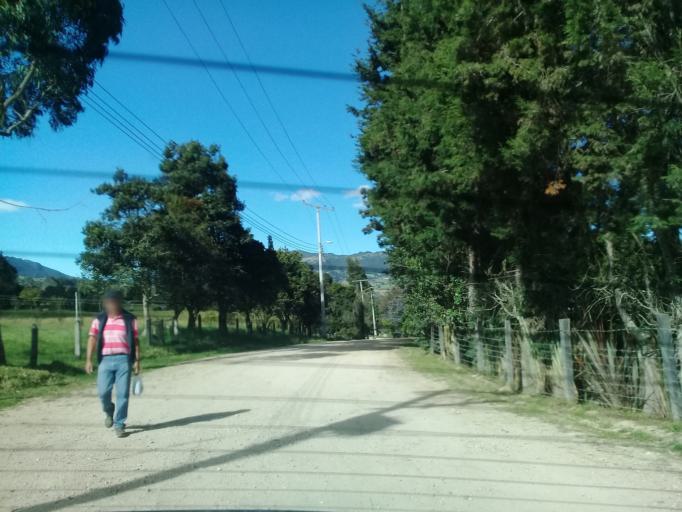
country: CO
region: Cundinamarca
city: Zipaquira
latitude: 4.9989
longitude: -74.0702
